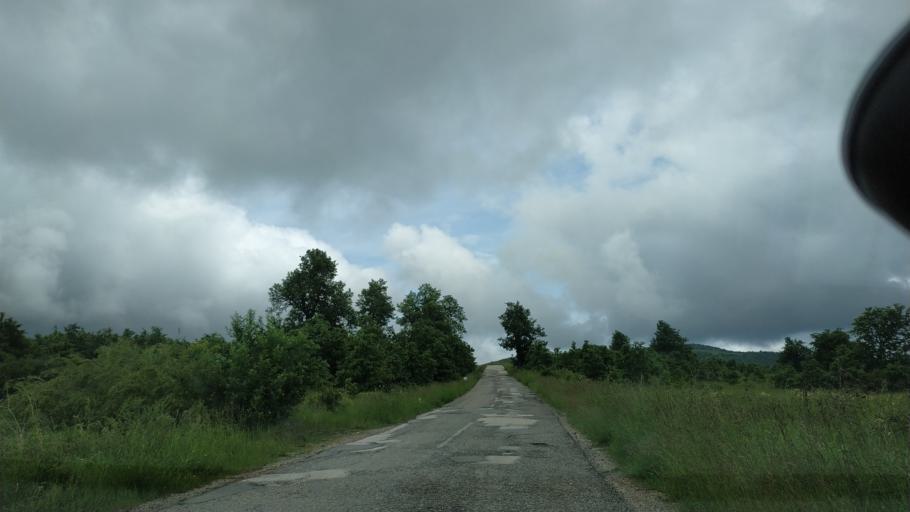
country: RS
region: Central Serbia
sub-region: Zajecarski Okrug
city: Soko Banja
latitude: 43.7021
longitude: 21.9353
